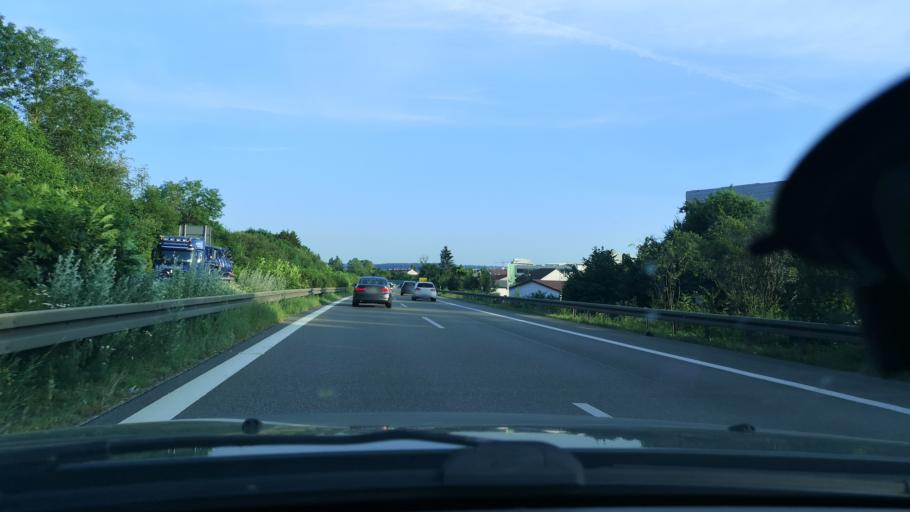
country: DE
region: Baden-Wuerttemberg
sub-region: Regierungsbezirk Stuttgart
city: Goeppingen
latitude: 48.6939
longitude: 9.6589
